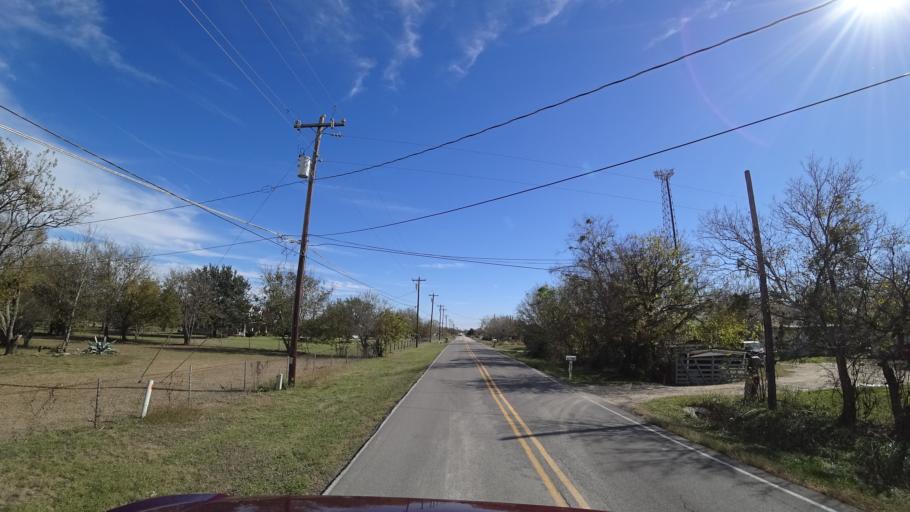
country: US
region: Texas
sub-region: Travis County
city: Onion Creek
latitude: 30.1157
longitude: -97.7039
